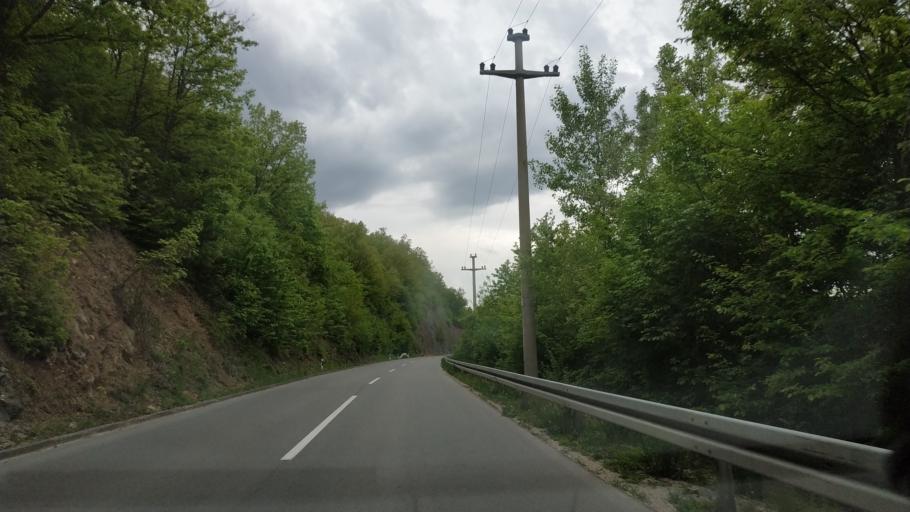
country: RS
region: Central Serbia
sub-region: Nisavski Okrug
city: Aleksinac
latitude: 43.6544
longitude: 21.7185
